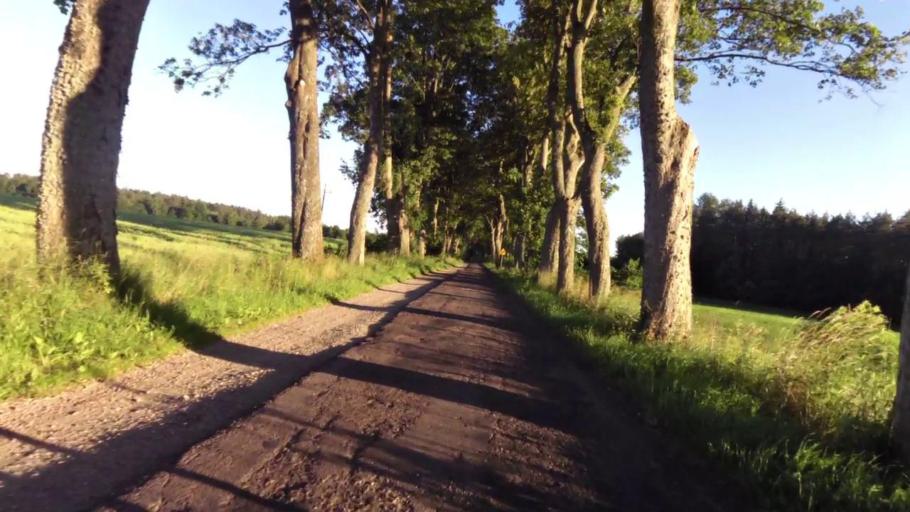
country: PL
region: West Pomeranian Voivodeship
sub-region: Koszalin
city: Koszalin
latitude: 54.0686
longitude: 16.1250
